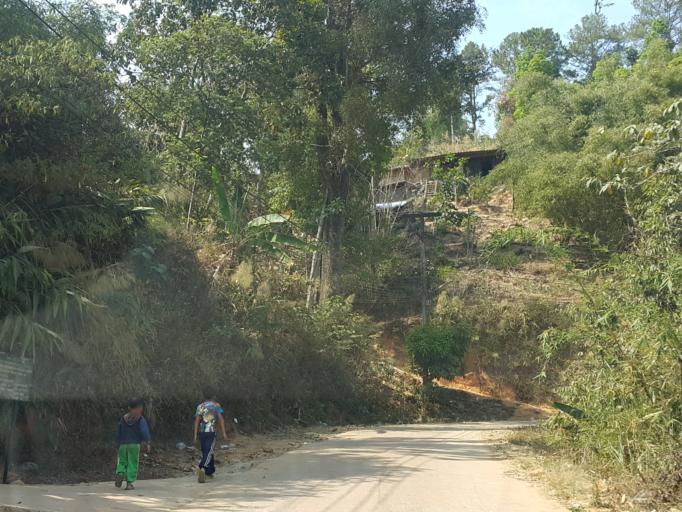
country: TH
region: Chiang Mai
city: Samoeng
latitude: 18.8852
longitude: 98.7849
